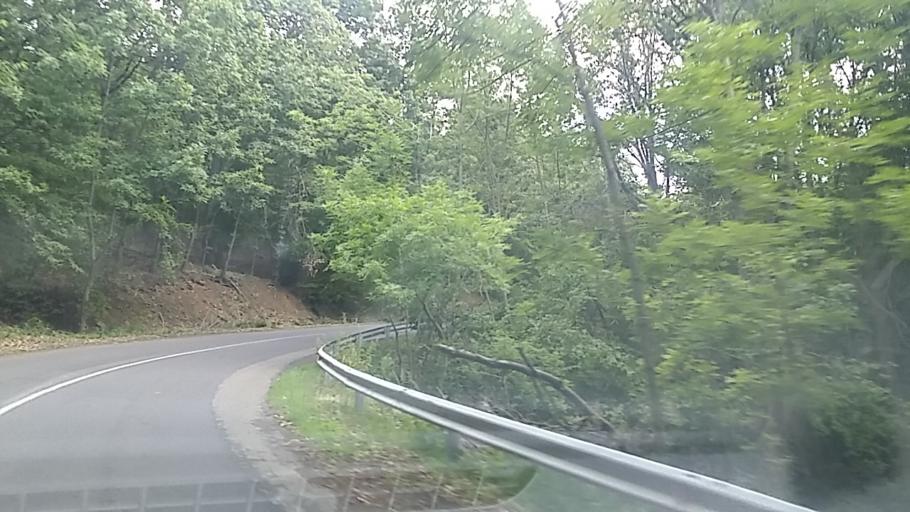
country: HU
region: Nograd
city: Batonyterenye
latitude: 47.9013
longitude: 19.8390
